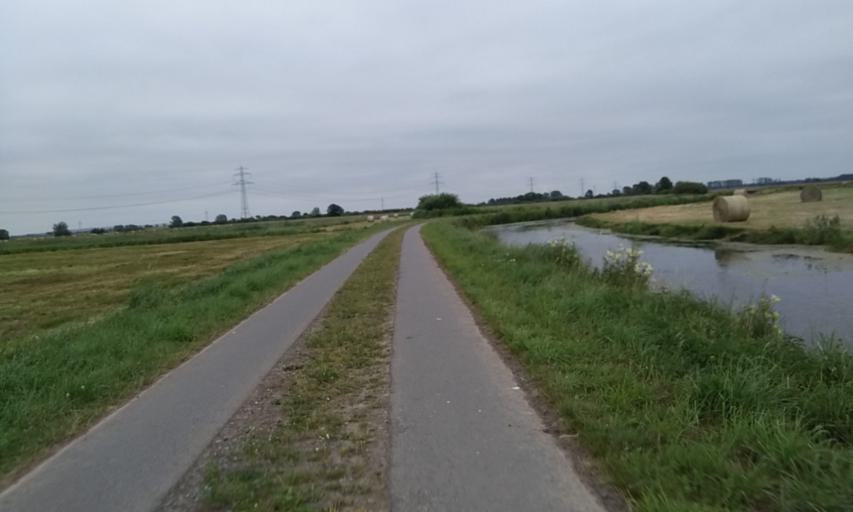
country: DE
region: Lower Saxony
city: Neuenkirchen
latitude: 53.5069
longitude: 9.6093
